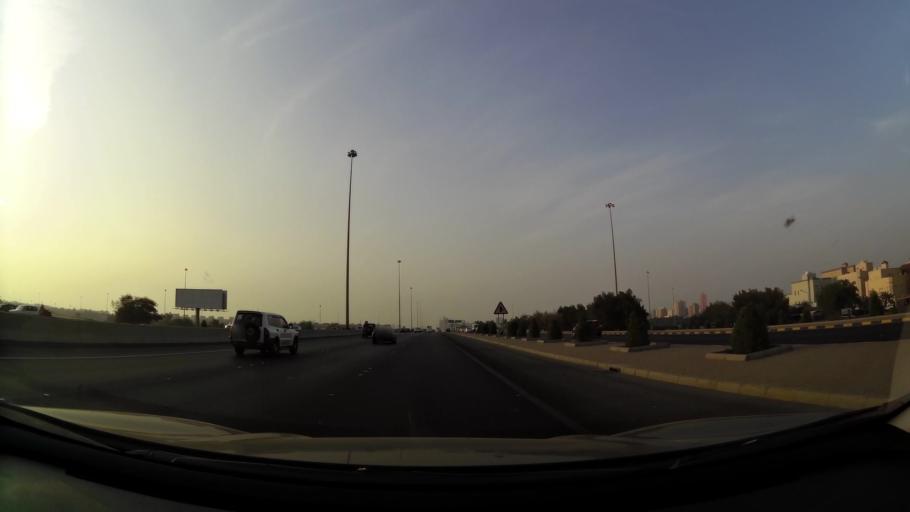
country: KW
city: Bayan
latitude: 29.3116
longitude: 48.0552
